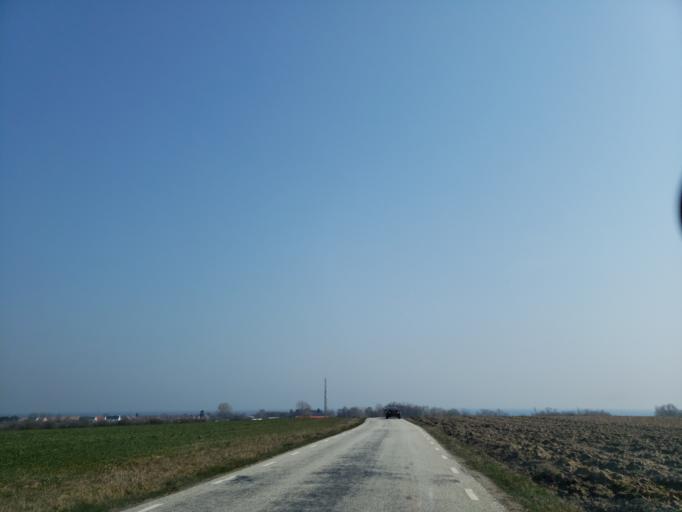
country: SE
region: Skane
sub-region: Simrishamns Kommun
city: Simrishamn
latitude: 55.5111
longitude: 14.3306
